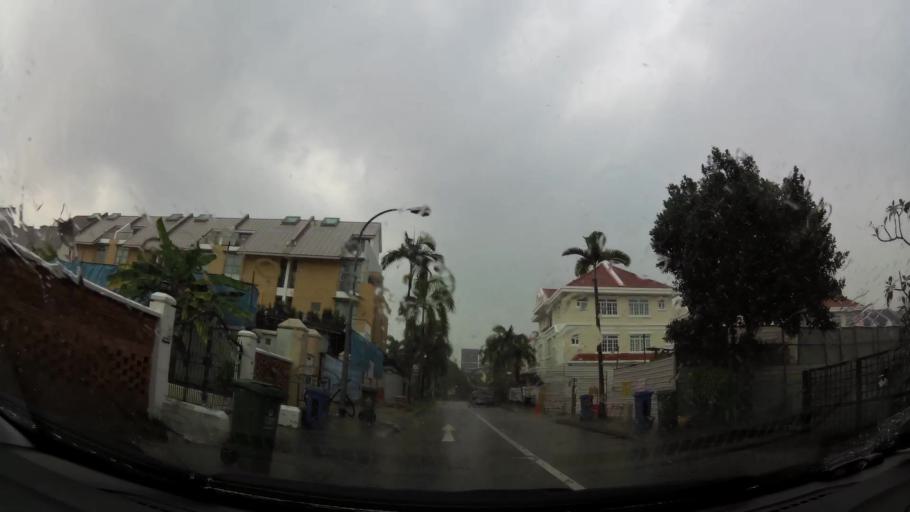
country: SG
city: Singapore
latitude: 1.3392
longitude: 103.9541
